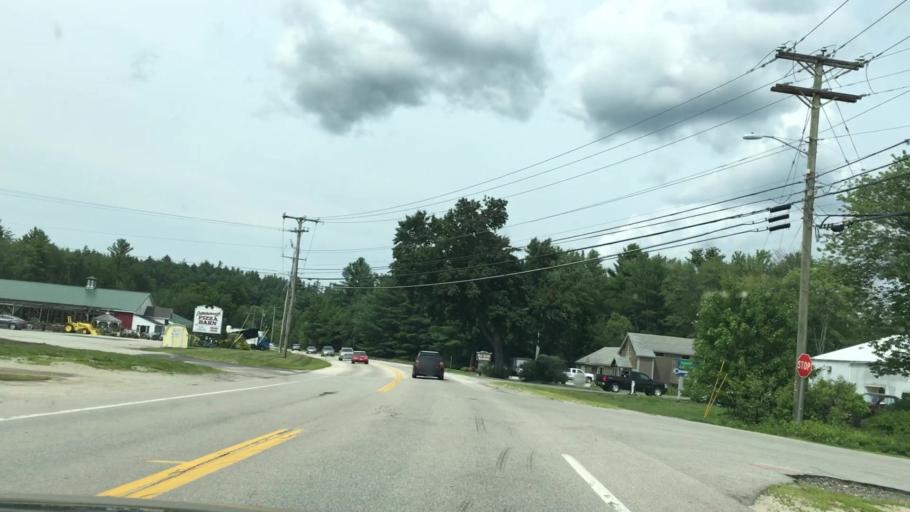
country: US
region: New Hampshire
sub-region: Hillsborough County
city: Peterborough
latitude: 42.8545
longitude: -71.9638
